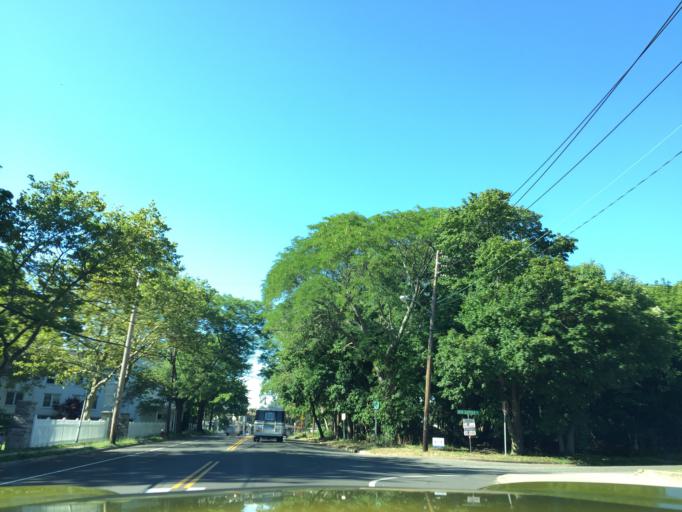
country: US
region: New York
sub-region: Suffolk County
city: Mattituck
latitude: 40.9897
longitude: -72.5343
